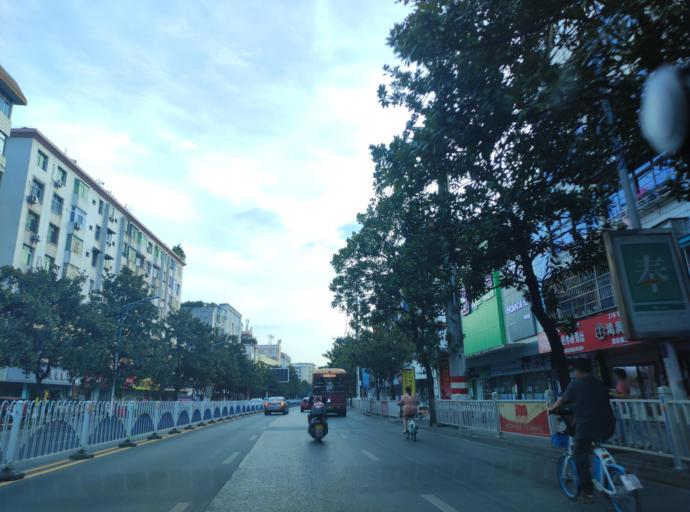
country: CN
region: Jiangxi Sheng
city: Pingxiang
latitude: 27.6329
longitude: 113.8546
